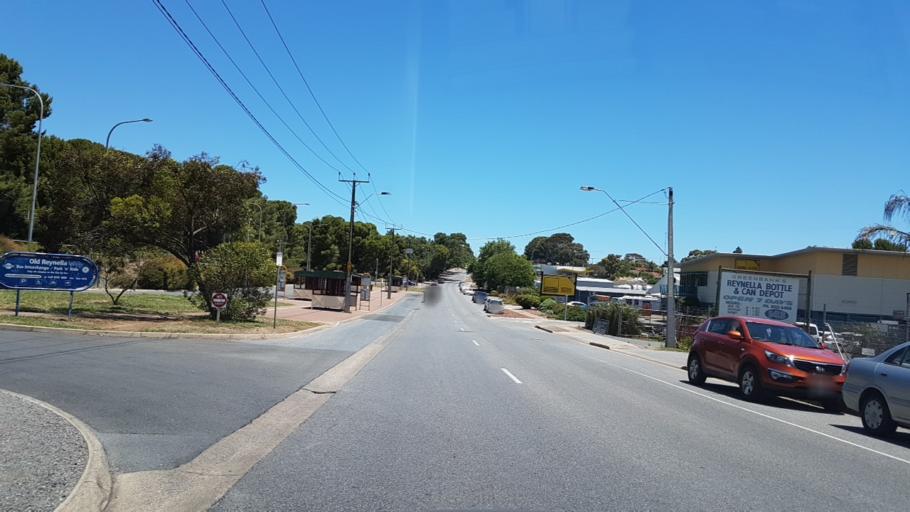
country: AU
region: South Australia
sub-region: Onkaparinga
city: Reynella
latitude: -35.0947
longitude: 138.5385
